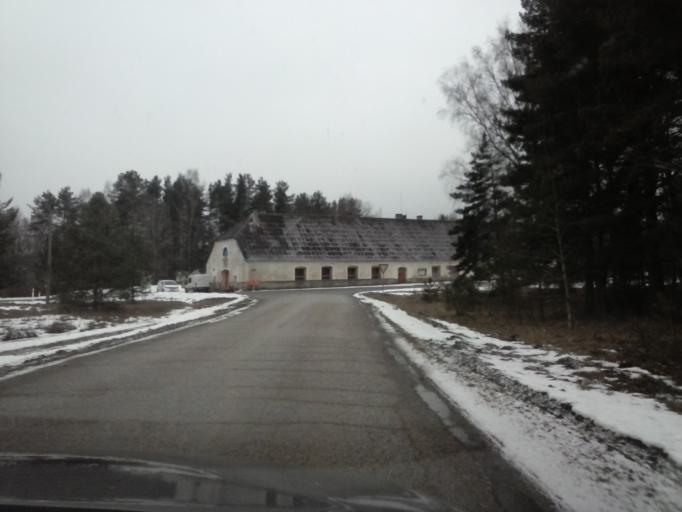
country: EE
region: Vorumaa
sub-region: Antsla vald
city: Vana-Antsla
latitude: 57.6148
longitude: 26.3995
